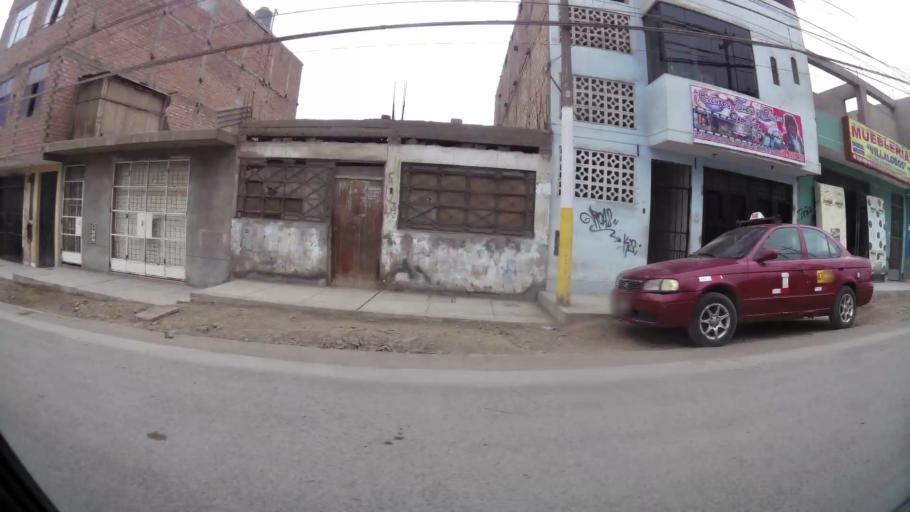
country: PE
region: Lima
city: Ventanilla
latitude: -11.9203
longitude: -77.0848
